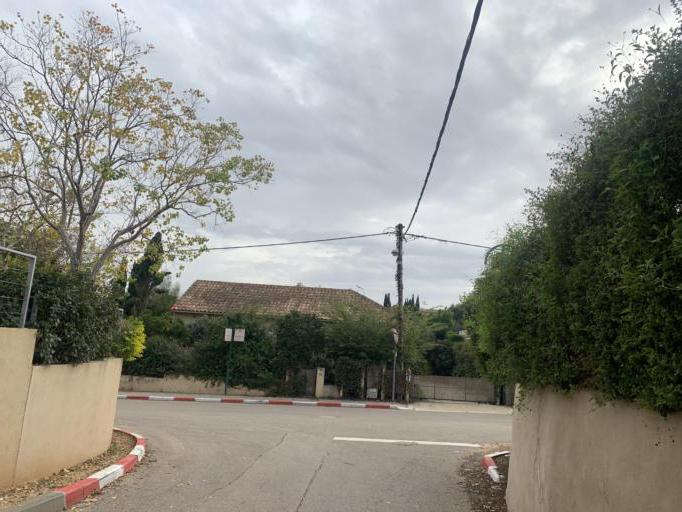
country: IL
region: Central District
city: Hod HaSharon
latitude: 32.1645
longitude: 34.8820
